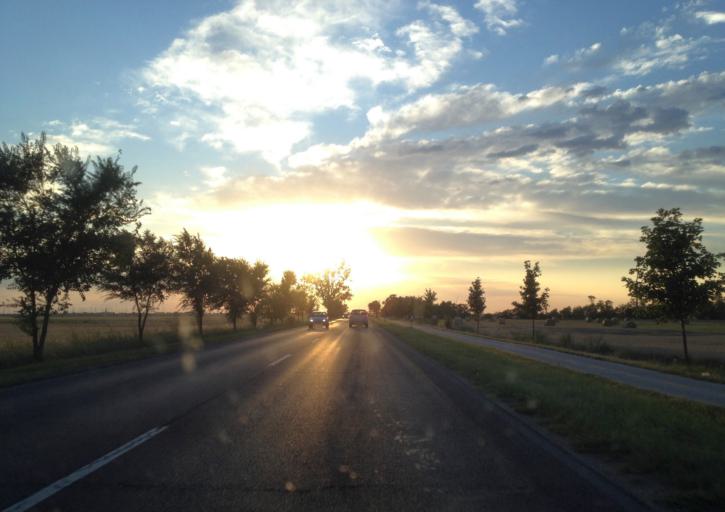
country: HU
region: Gyor-Moson-Sopron
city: Mosonmagyarovar
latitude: 47.8877
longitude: 17.2336
